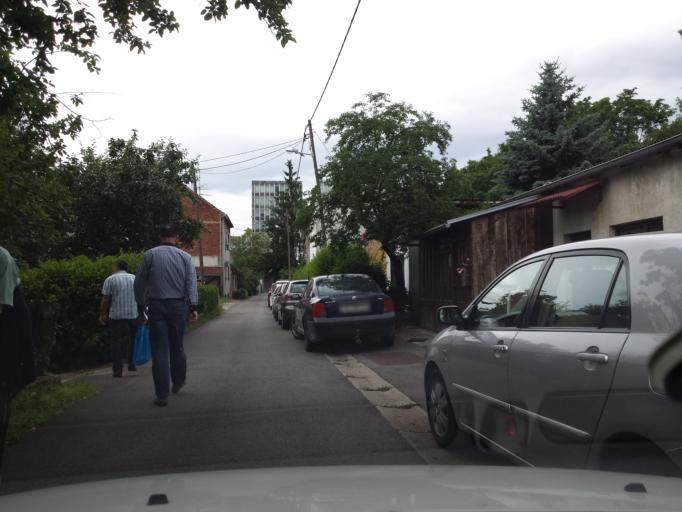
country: HR
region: Grad Zagreb
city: Zagreb - Centar
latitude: 45.8001
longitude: 15.9843
